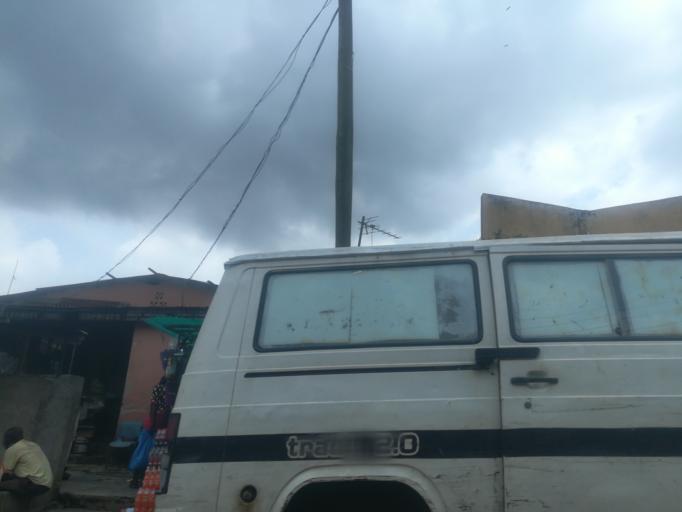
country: NG
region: Lagos
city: Somolu
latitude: 6.5565
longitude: 3.3930
